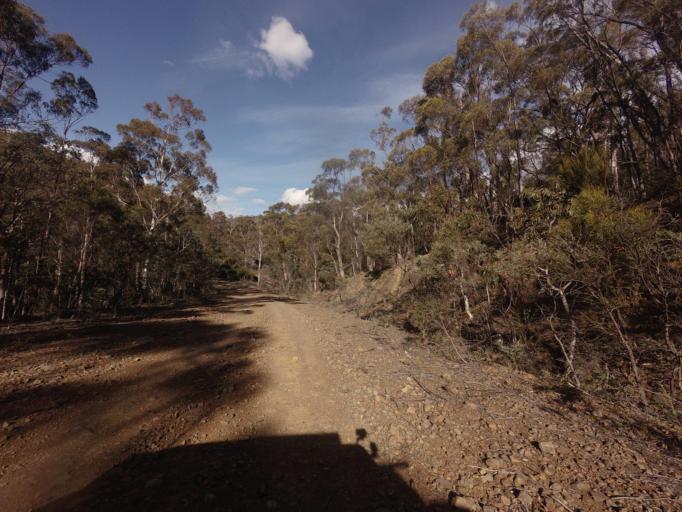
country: AU
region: Tasmania
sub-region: Break O'Day
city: St Helens
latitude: -41.8548
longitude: 148.0385
